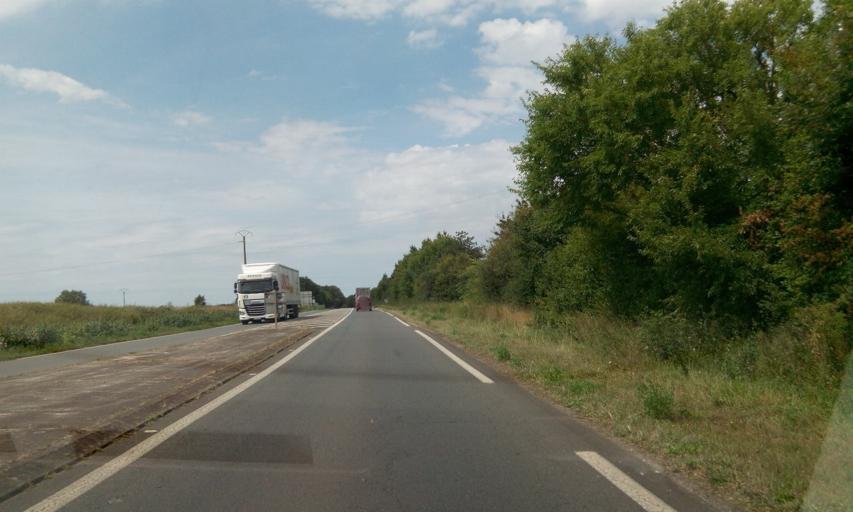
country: FR
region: Poitou-Charentes
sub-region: Departement des Deux-Sevres
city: Celles-sur-Belle
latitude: 46.2529
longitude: -0.1994
